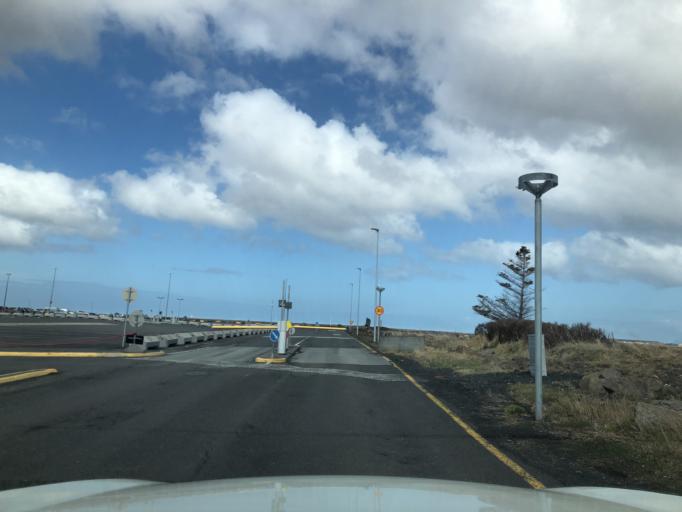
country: IS
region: Southern Peninsula
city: Reykjanesbaer
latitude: 63.9966
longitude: -22.6186
